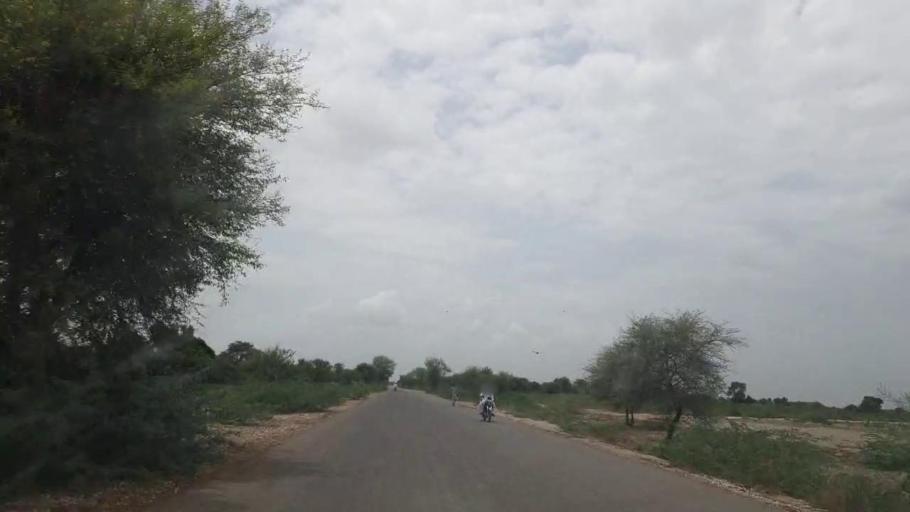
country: PK
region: Sindh
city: Naukot
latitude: 24.8909
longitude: 69.2534
